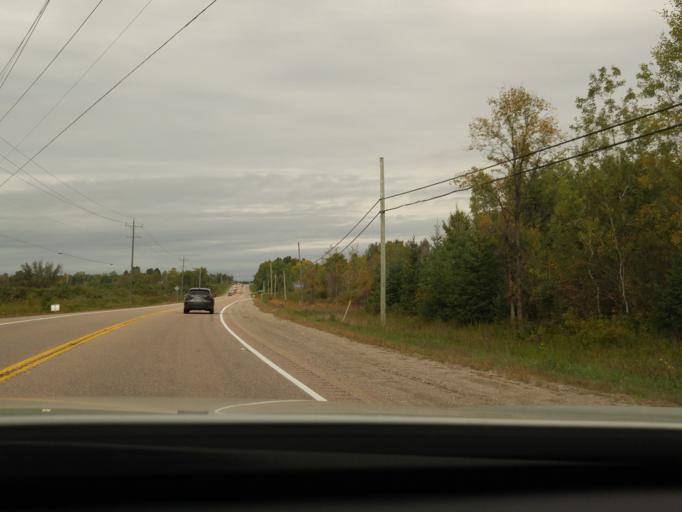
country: CA
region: Ontario
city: Renfrew
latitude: 45.5732
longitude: -76.8134
